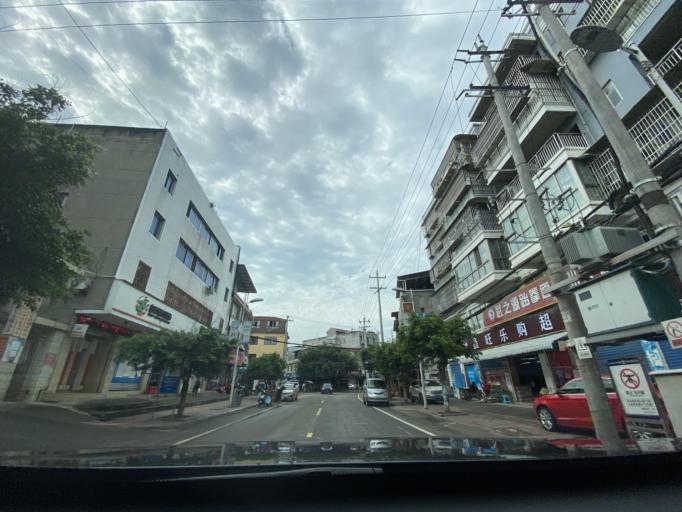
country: CN
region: Sichuan
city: Jiancheng
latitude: 30.4314
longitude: 104.6379
